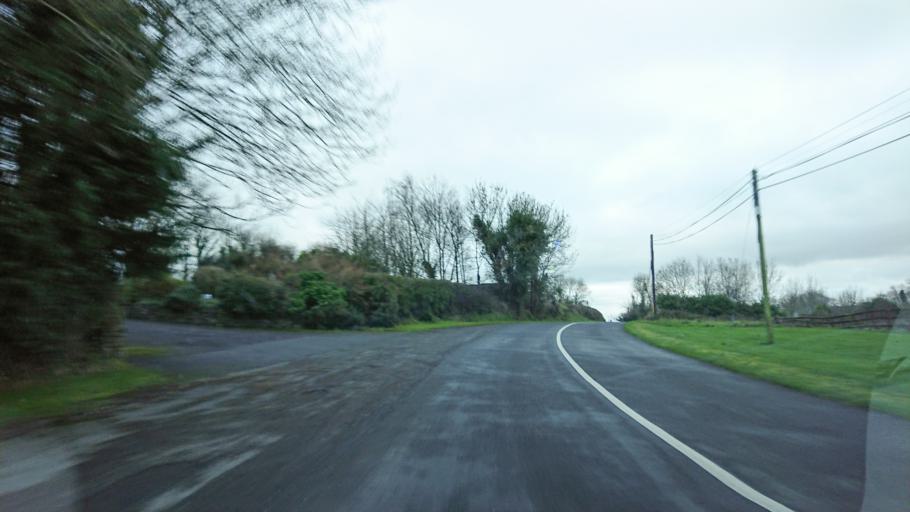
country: IE
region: Munster
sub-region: Waterford
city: Portlaw
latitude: 52.1869
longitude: -7.4086
